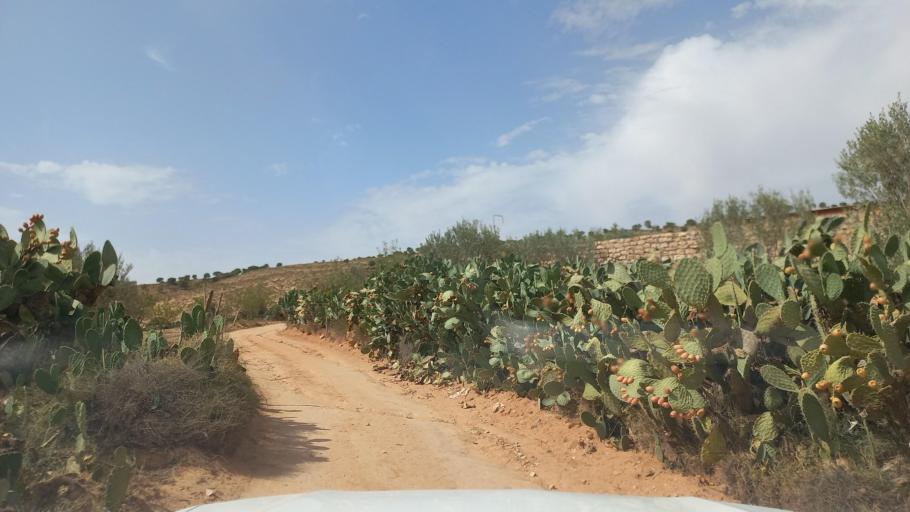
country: TN
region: Al Qasrayn
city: Kasserine
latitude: 35.3706
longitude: 8.8797
